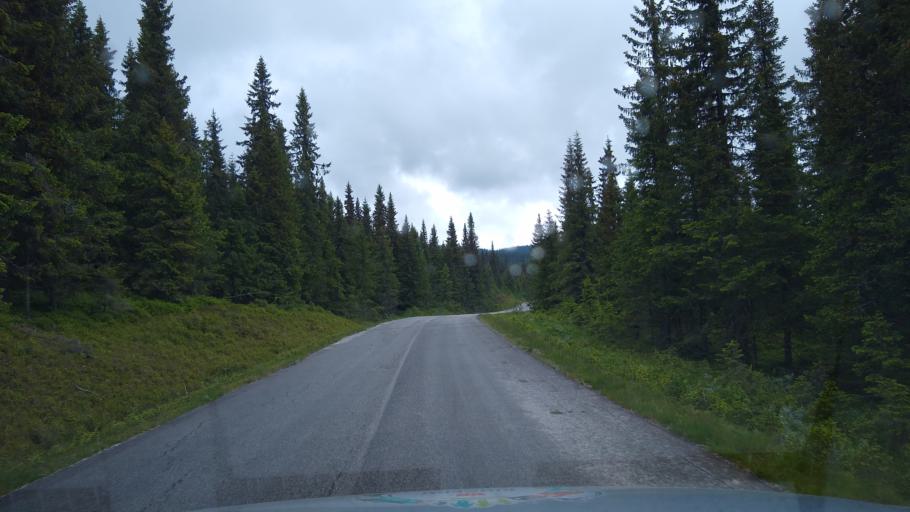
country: NO
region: Oppland
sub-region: Ringebu
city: Ringebu
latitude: 61.4870
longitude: 10.1147
